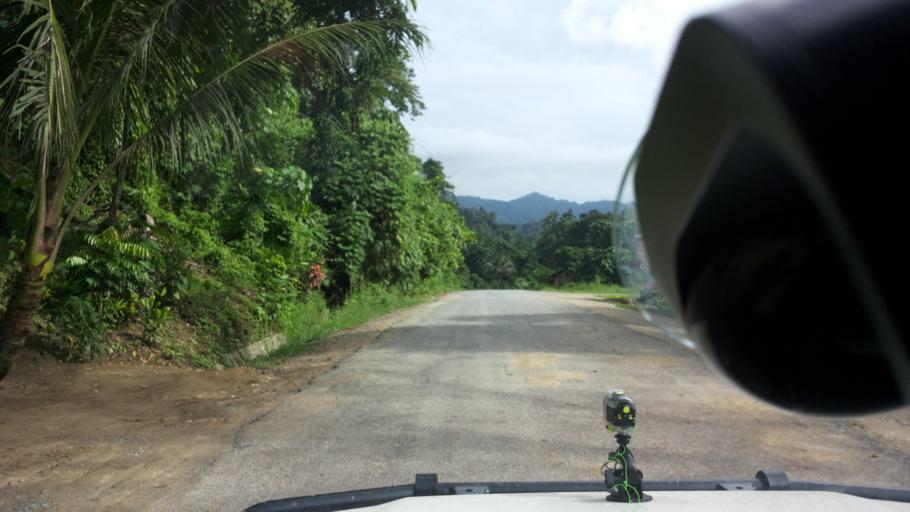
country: PG
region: Madang
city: Madang
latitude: -5.3966
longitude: 145.6292
